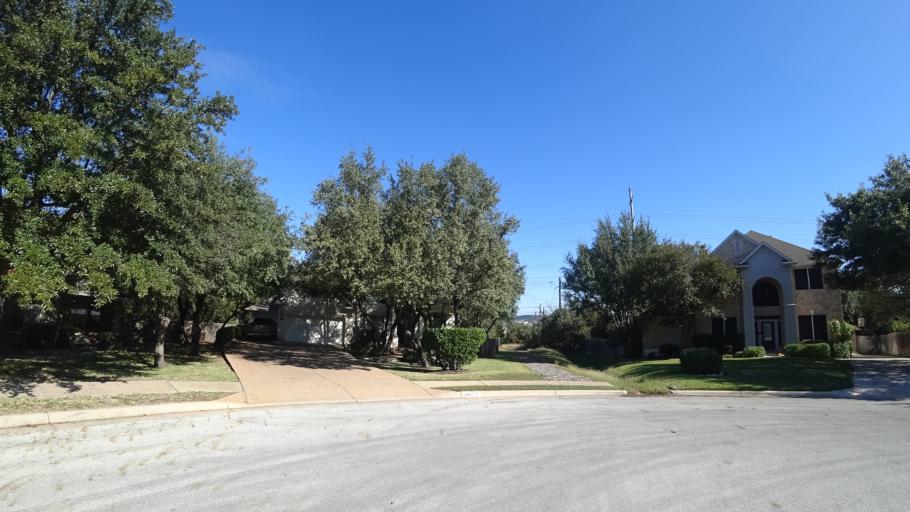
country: US
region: Texas
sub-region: Travis County
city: Hudson Bend
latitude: 30.3790
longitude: -97.8978
